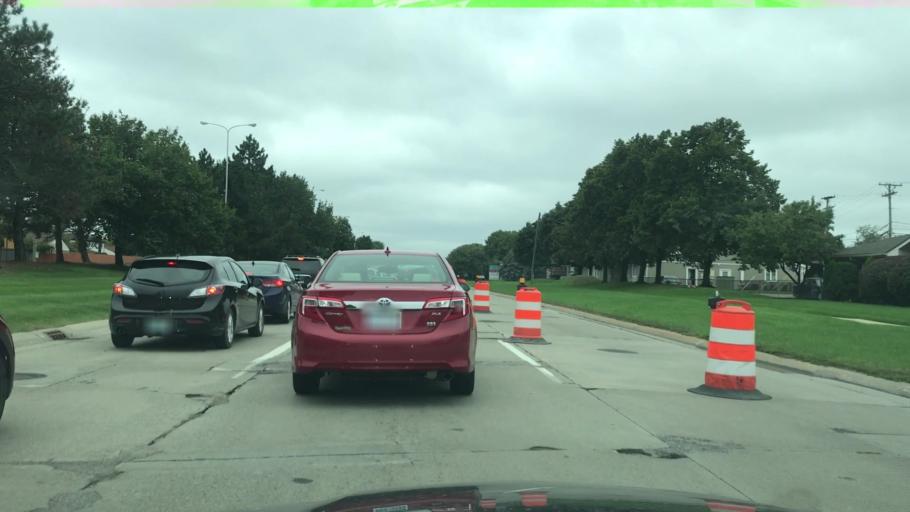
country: US
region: Michigan
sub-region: Macomb County
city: Sterling Heights
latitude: 42.5649
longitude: -83.0639
